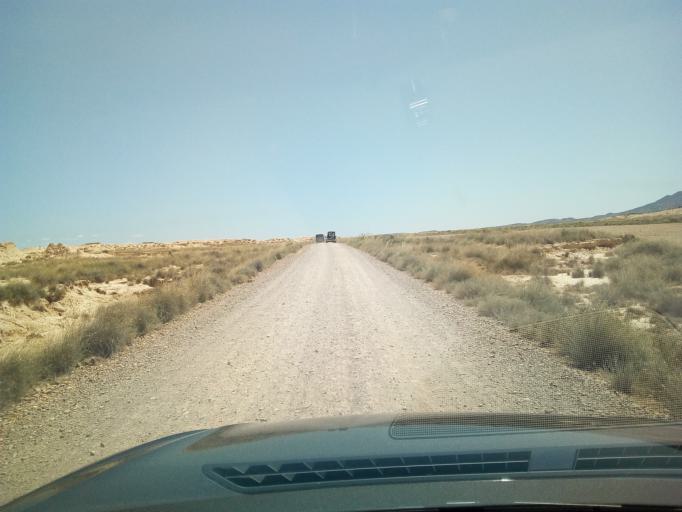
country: ES
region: Navarre
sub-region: Provincia de Navarra
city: Arguedas
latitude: 42.1821
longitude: -1.4687
